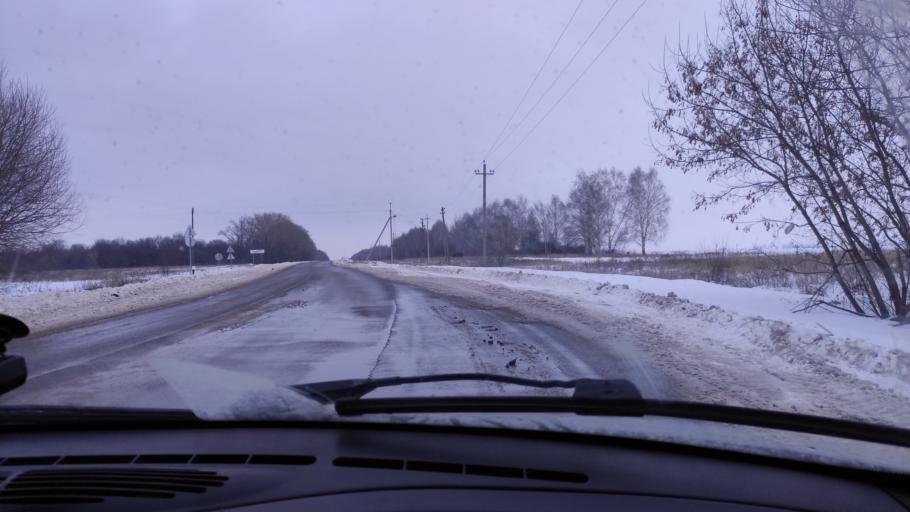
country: RU
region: Tambov
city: Pervomayskiy
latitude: 53.3037
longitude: 40.3819
